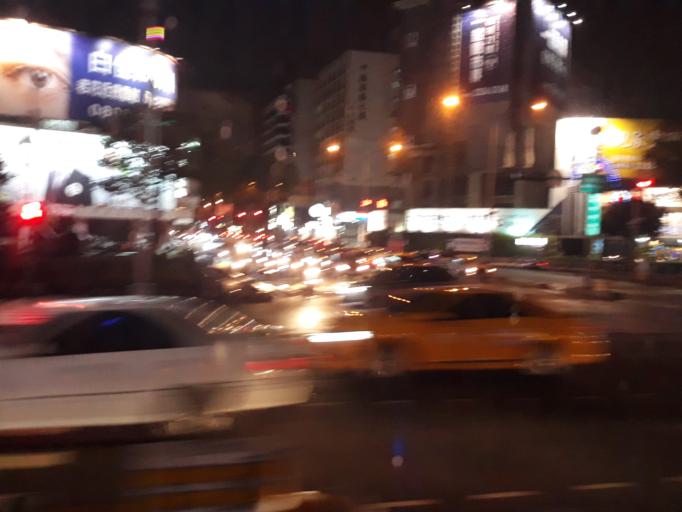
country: TW
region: Taiwan
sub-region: Taichung City
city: Taichung
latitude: 24.1569
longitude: 120.6599
